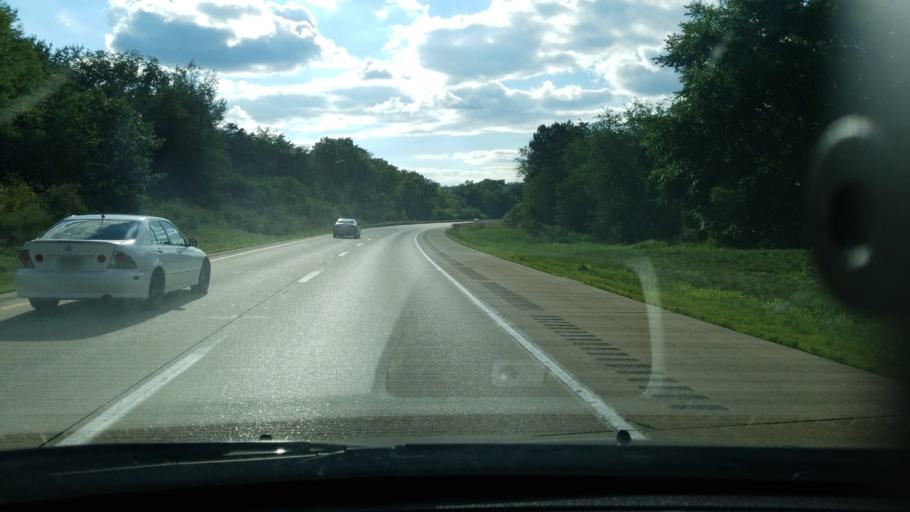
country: US
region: Pennsylvania
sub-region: Northumberland County
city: Milton
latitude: 40.9932
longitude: -76.7379
